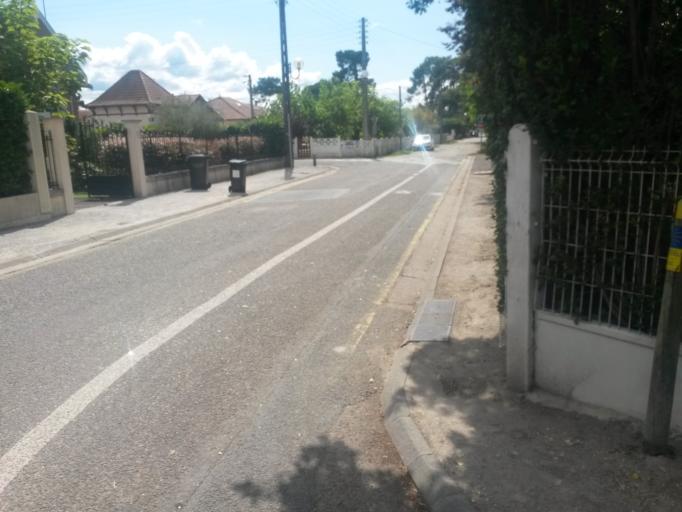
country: FR
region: Aquitaine
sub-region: Departement de la Gironde
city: Andernos-les-Bains
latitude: 44.7388
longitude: -1.0955
